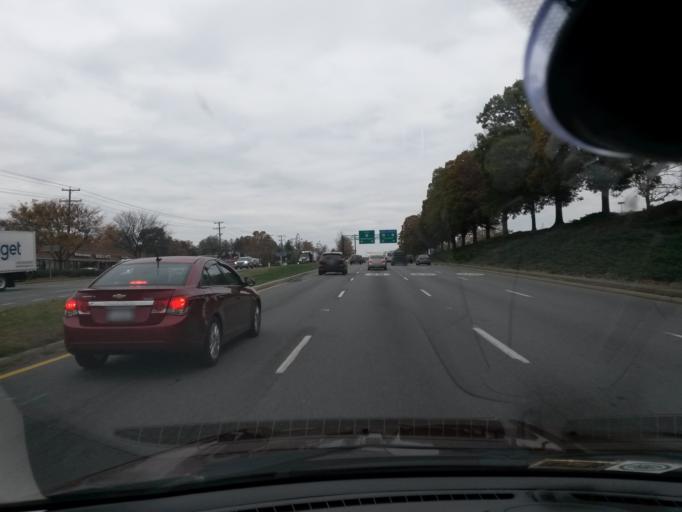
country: US
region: Virginia
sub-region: City of Charlottesville
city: Charlottesville
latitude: 38.0773
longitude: -78.4778
